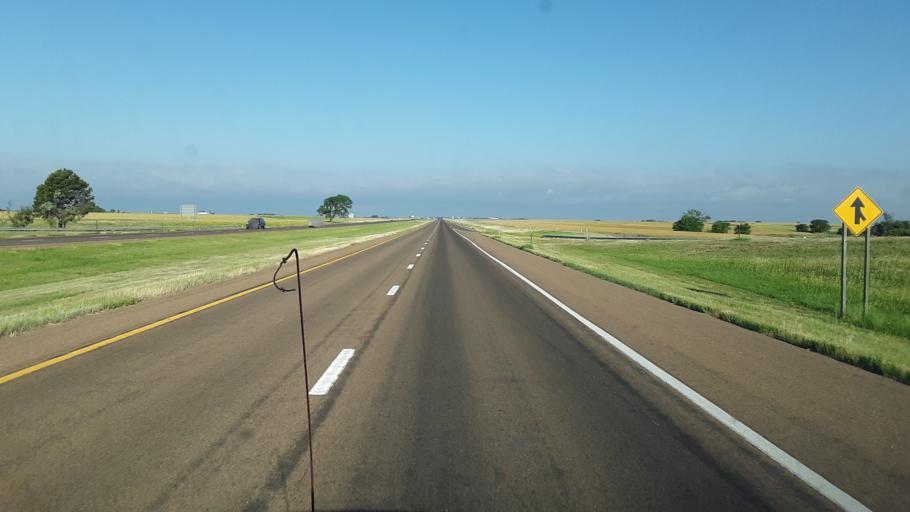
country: US
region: Kansas
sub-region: Ellis County
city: Victoria
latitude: 38.8638
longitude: -99.0209
